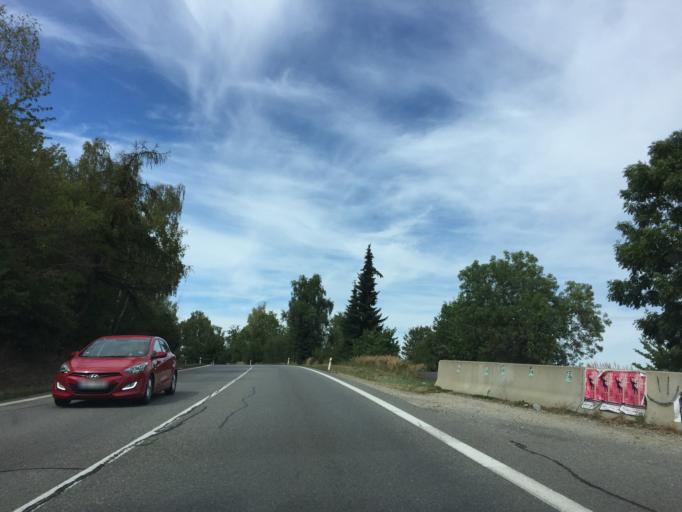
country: CZ
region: Jihocesky
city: Chotoviny
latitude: 49.5542
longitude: 14.6664
